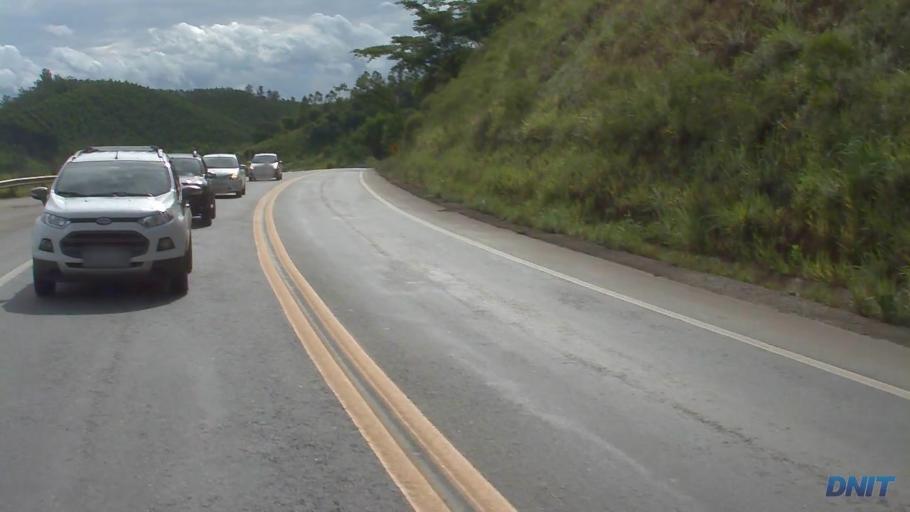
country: BR
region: Minas Gerais
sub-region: Belo Oriente
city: Belo Oriente
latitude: -19.2659
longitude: -42.3524
